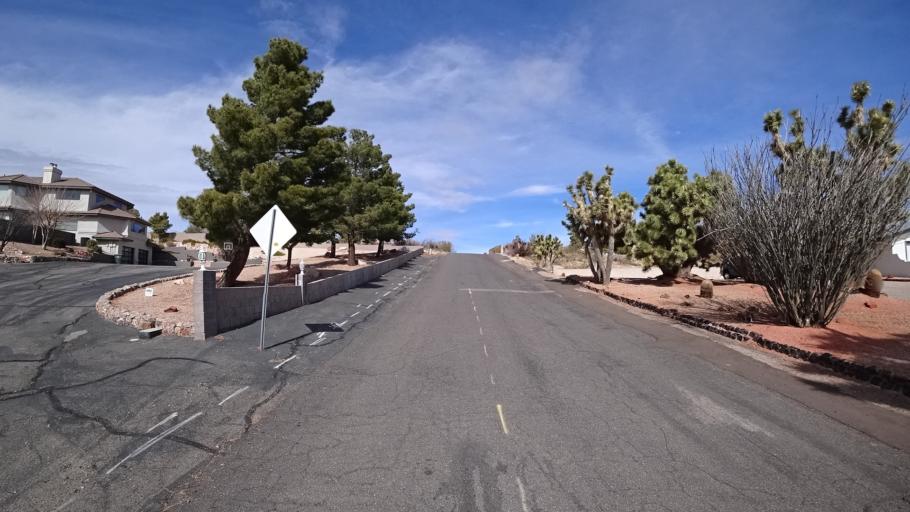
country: US
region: Arizona
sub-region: Mohave County
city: New Kingman-Butler
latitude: 35.2326
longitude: -114.0535
